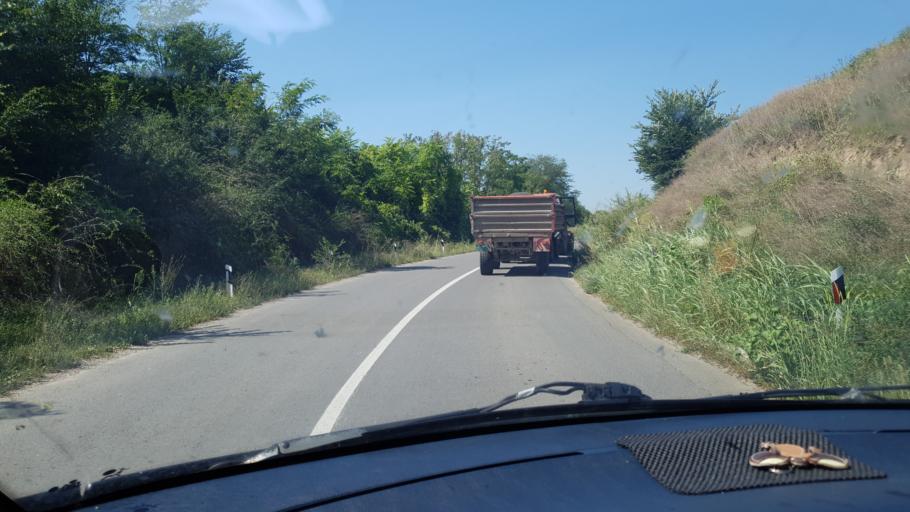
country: RS
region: Autonomna Pokrajina Vojvodina
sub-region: Juznobacki Okrug
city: Kovilj
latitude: 45.2232
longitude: 20.0426
